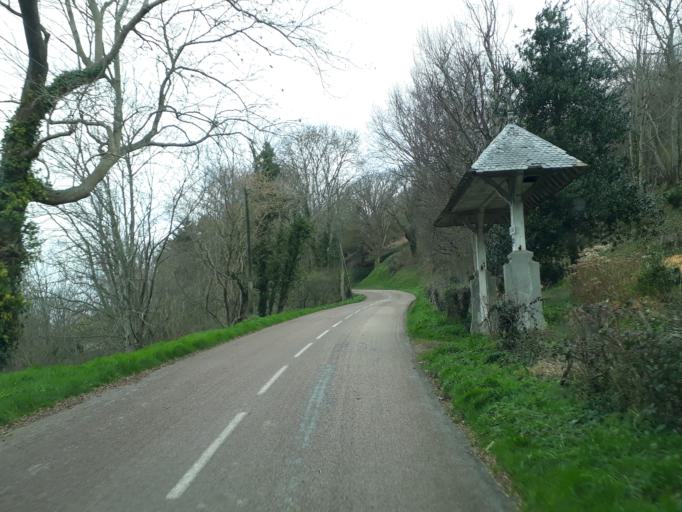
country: FR
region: Haute-Normandie
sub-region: Departement de la Seine-Maritime
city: Yport
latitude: 49.7349
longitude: 0.2925
